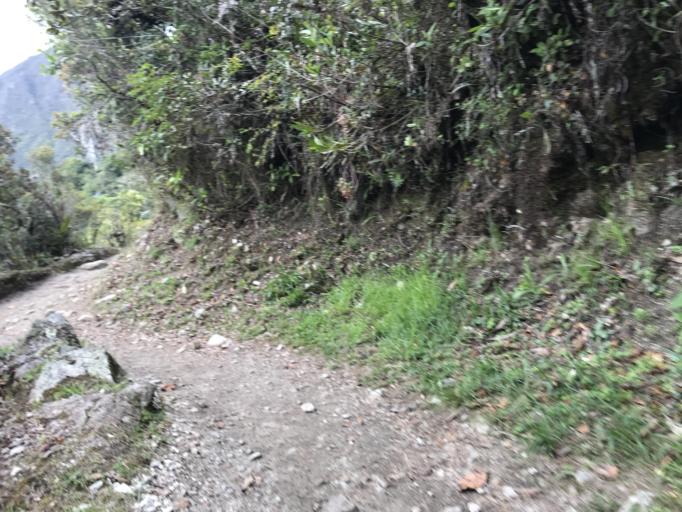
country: PE
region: Cusco
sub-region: Provincia de La Convencion
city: Santa Teresa
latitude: -13.1881
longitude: -72.5387
